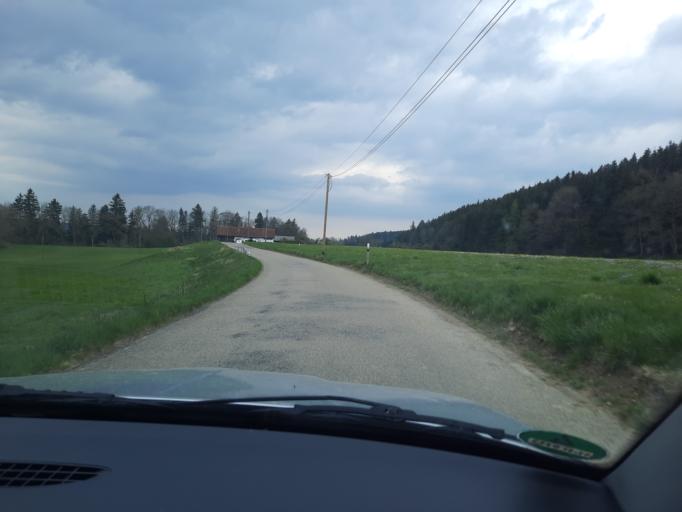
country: DE
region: Bavaria
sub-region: Swabia
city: Lautrach
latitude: 47.9240
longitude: 10.1194
